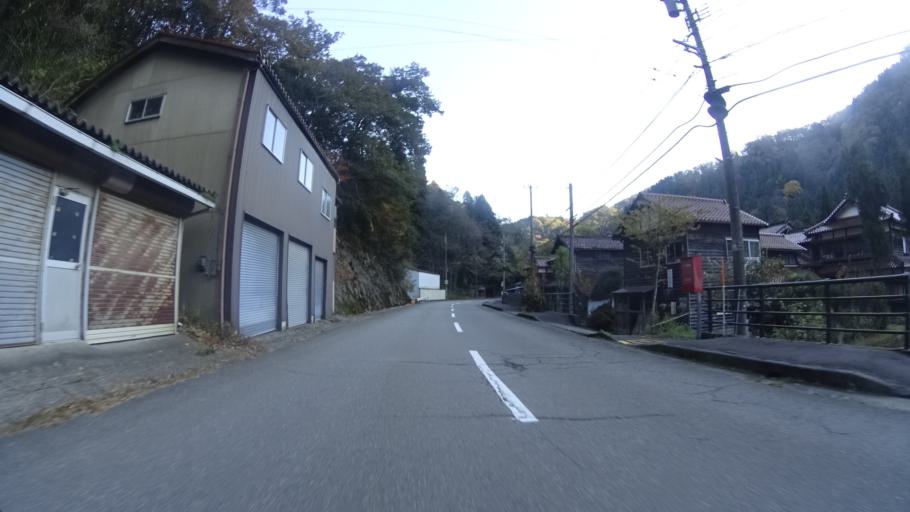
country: JP
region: Fukui
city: Maruoka
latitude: 36.2238
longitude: 136.3587
